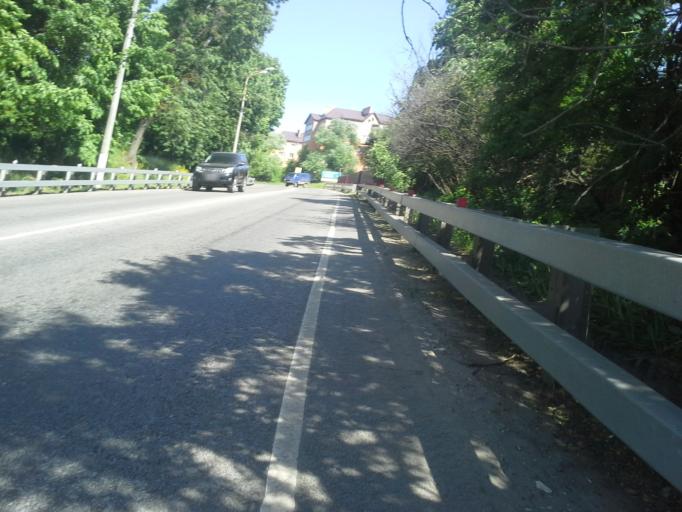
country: RU
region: Moskovskaya
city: Troitsk
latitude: 55.4244
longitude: 37.2908
